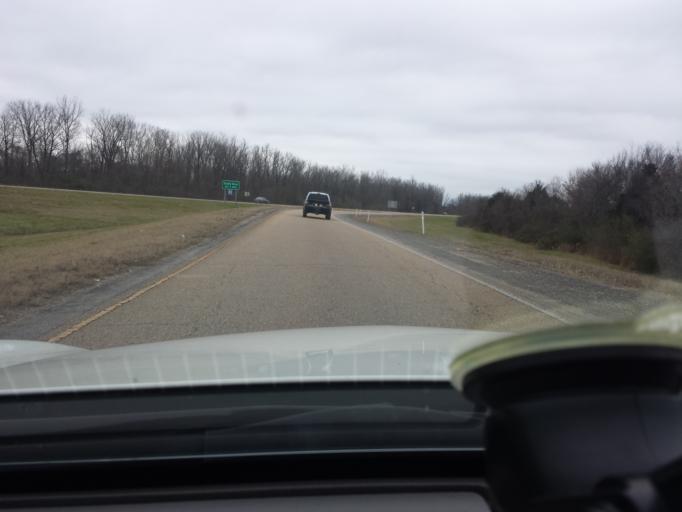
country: US
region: Mississippi
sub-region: Lee County
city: Tupelo
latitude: 34.2545
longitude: -88.6948
